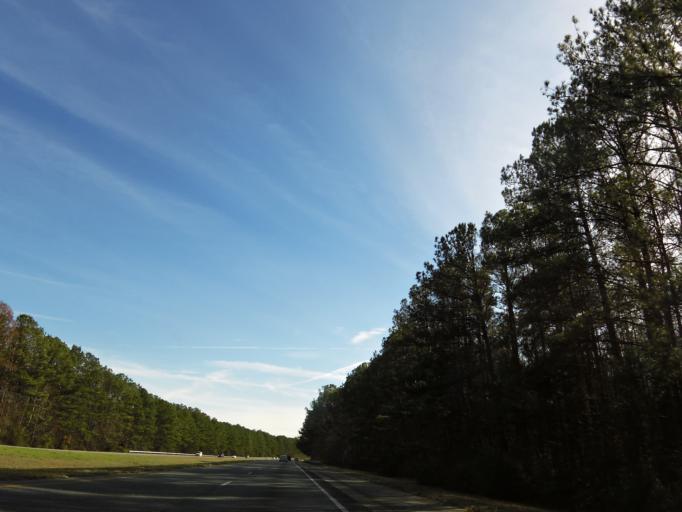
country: US
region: Georgia
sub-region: Harris County
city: Hamilton
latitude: 32.7632
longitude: -85.0183
